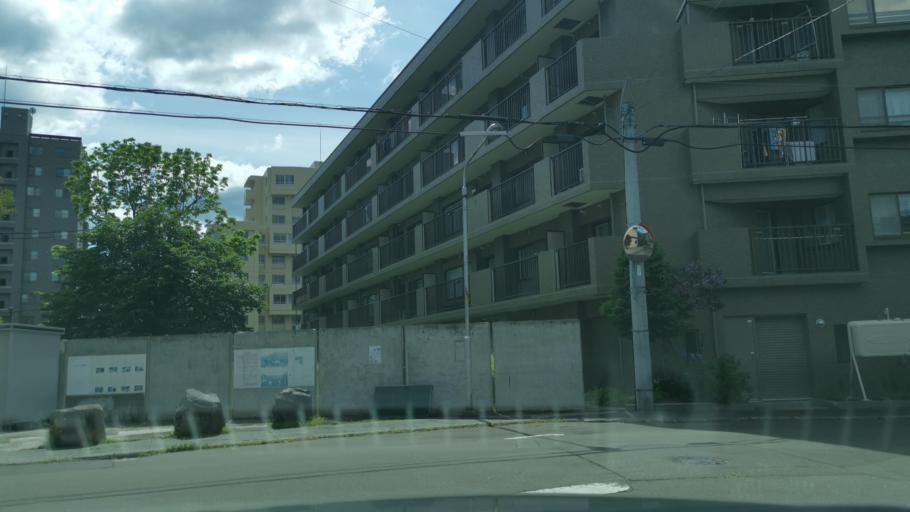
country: JP
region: Hokkaido
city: Sapporo
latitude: 43.0427
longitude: 141.3277
